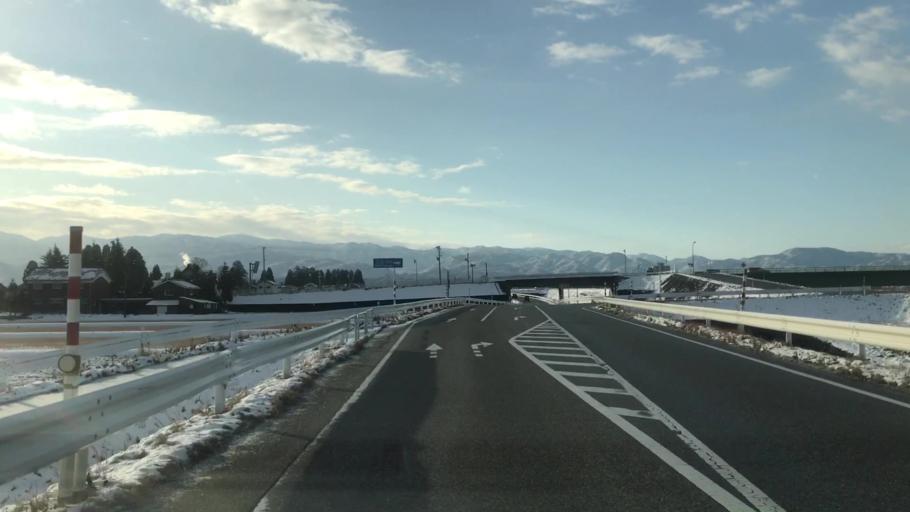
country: JP
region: Toyama
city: Toyama-shi
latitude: 36.6505
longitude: 137.2861
